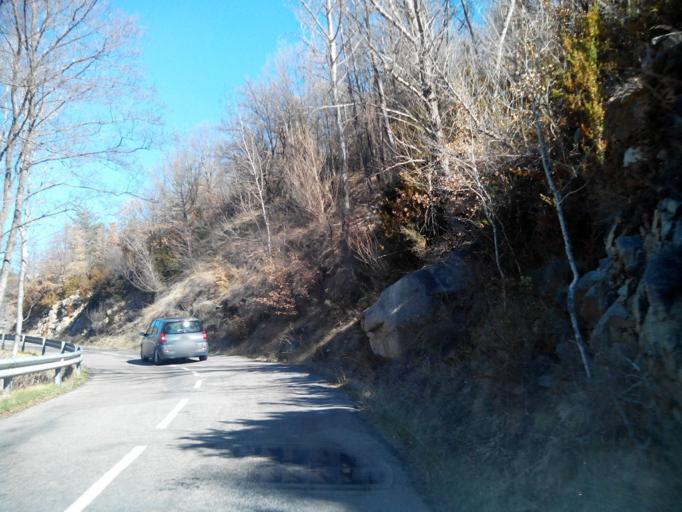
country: ES
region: Catalonia
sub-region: Provincia de Lleida
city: Lles de Cerdanya
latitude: 42.3643
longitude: 1.6854
